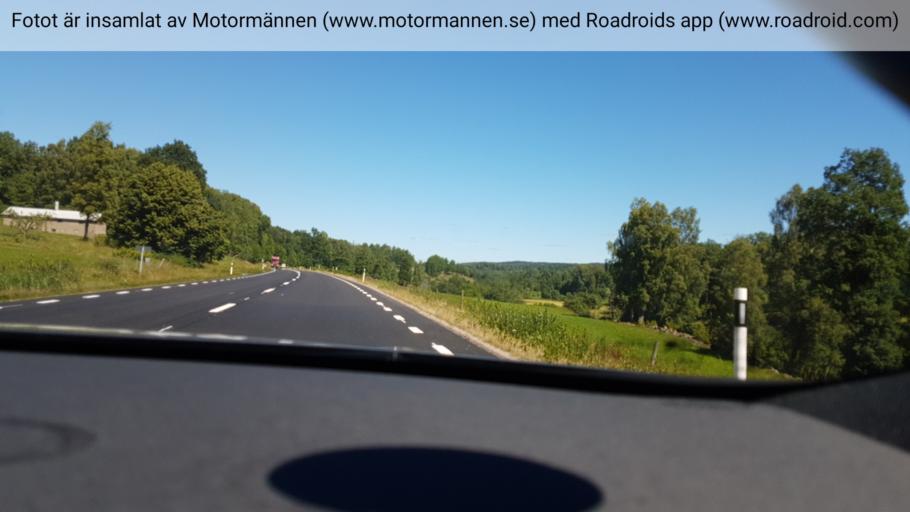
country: SE
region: Vaestra Goetaland
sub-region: Ulricehamns Kommun
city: Ulricehamn
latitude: 57.9065
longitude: 13.4746
